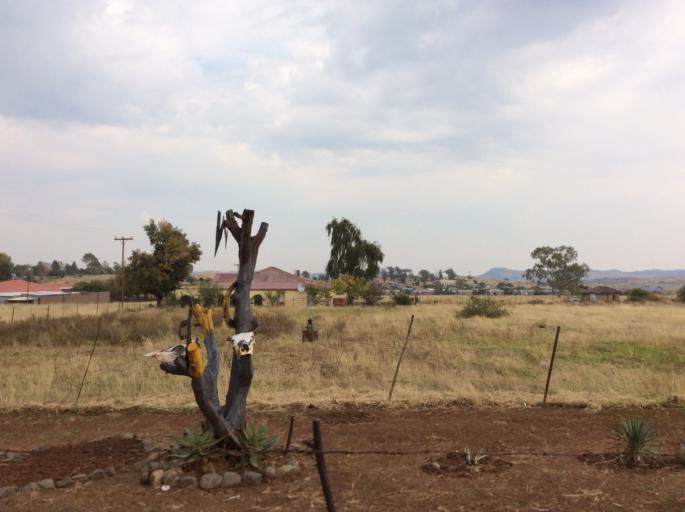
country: LS
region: Mafeteng
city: Mafeteng
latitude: -29.9853
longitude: 27.0132
